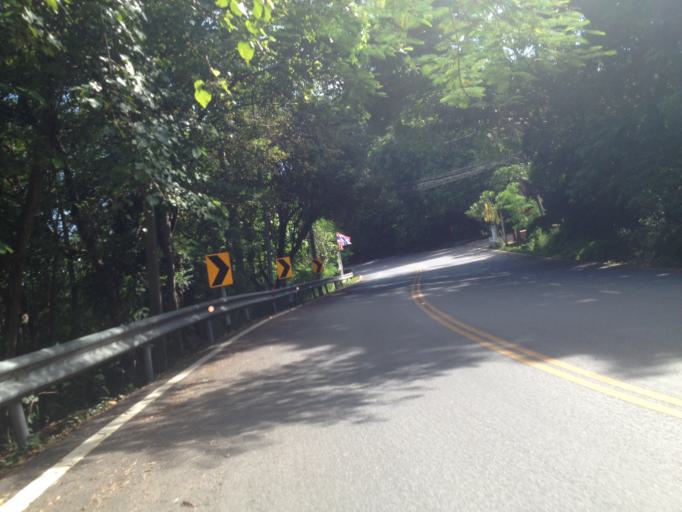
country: TH
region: Chiang Mai
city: Chiang Mai
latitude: 18.8159
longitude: 98.9464
